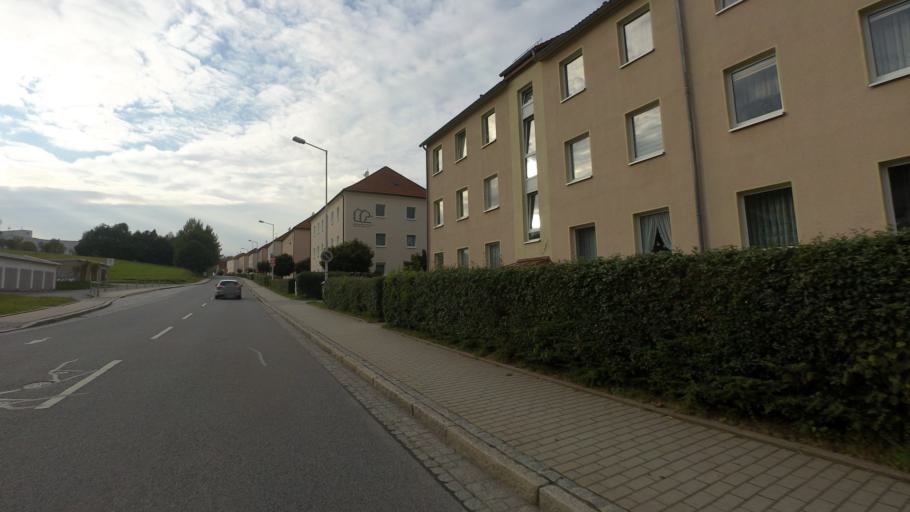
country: DE
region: Saxony
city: Sebnitz
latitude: 50.9829
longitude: 14.2712
